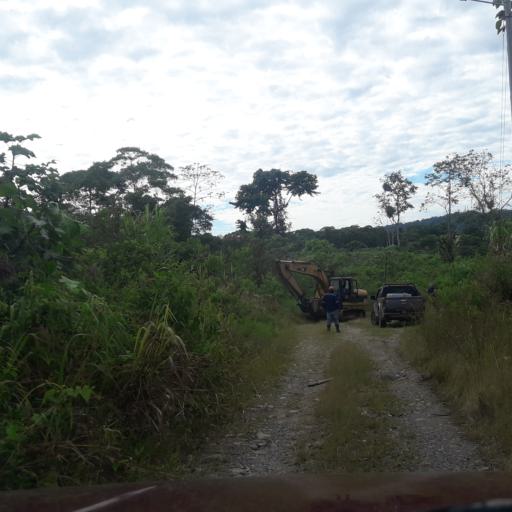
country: EC
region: Napo
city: Tena
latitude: -0.9812
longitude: -77.8238
